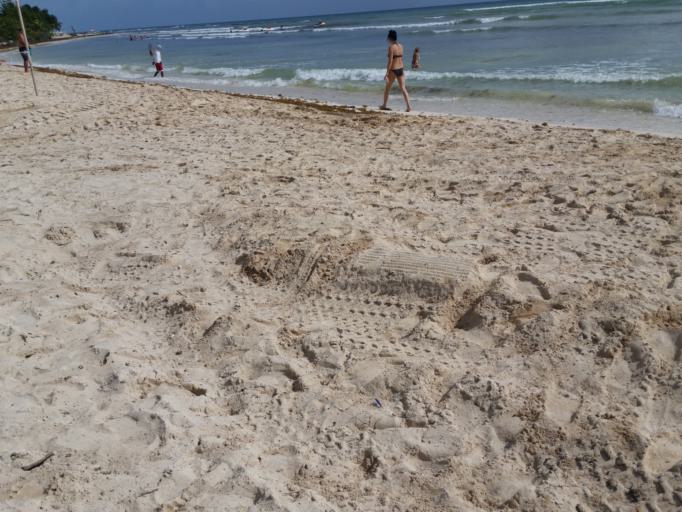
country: MX
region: Quintana Roo
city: Playa del Carmen
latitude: 20.6696
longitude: -87.0270
